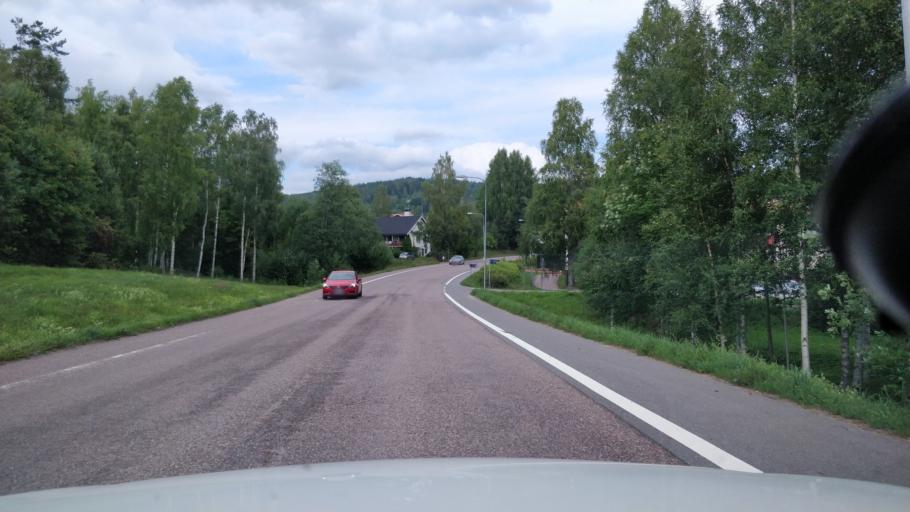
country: SE
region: Dalarna
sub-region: Faluns Kommun
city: Bjursas
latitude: 60.7365
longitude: 15.4401
